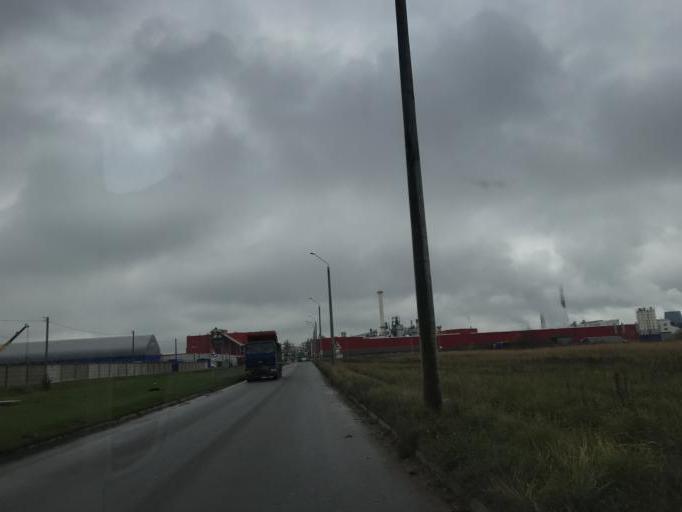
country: BY
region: Mogilev
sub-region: Mahilyowski Rayon
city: Veyno
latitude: 53.8256
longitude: 30.3525
